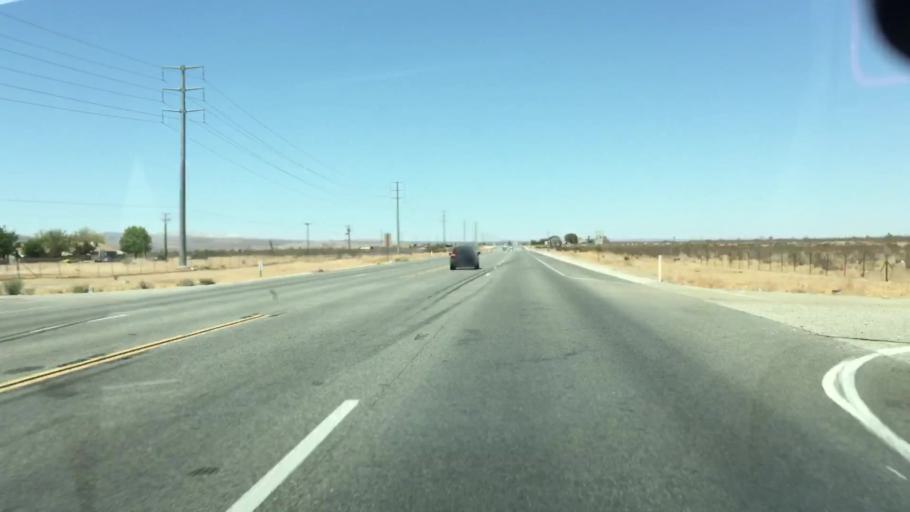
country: US
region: California
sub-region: San Bernardino County
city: Adelanto
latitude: 34.5935
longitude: -117.4168
